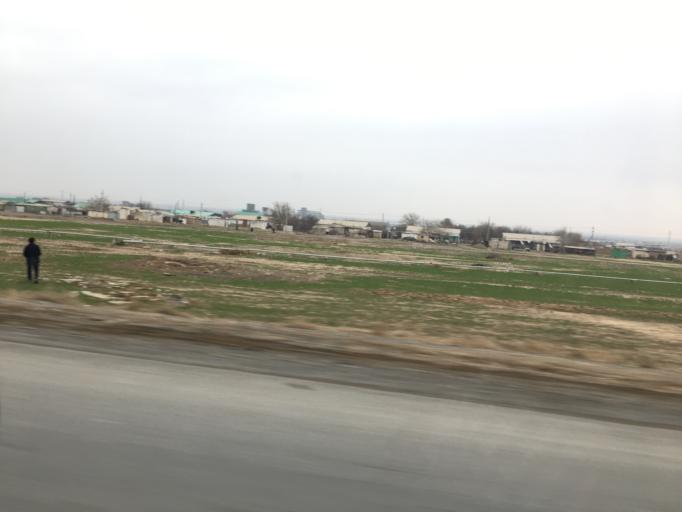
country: IR
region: Razavi Khorasan
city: Dargaz
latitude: 37.7657
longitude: 58.9032
